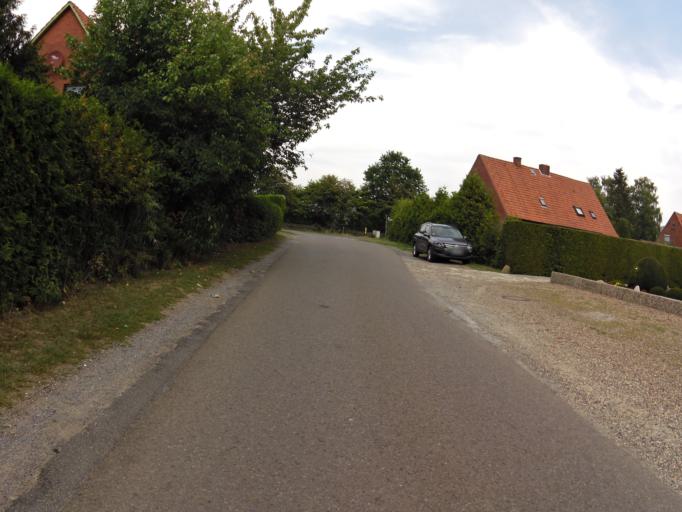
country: DE
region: Lower Saxony
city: Estorf
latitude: 52.5966
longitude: 9.1574
